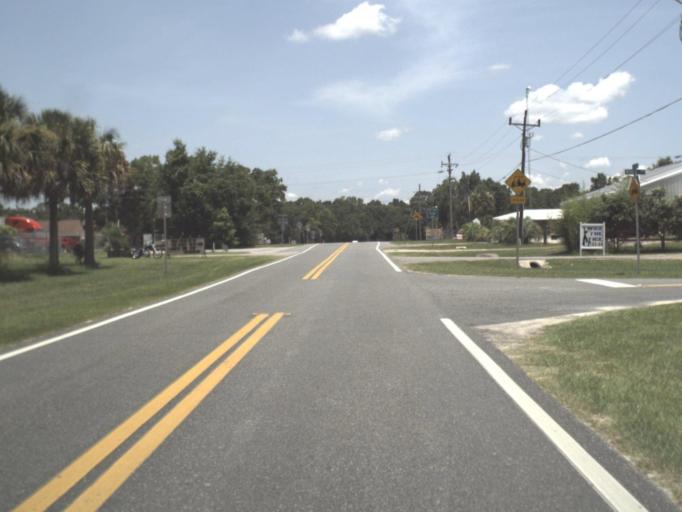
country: US
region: Florida
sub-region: Taylor County
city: Steinhatchee
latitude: 29.6718
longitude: -83.3698
